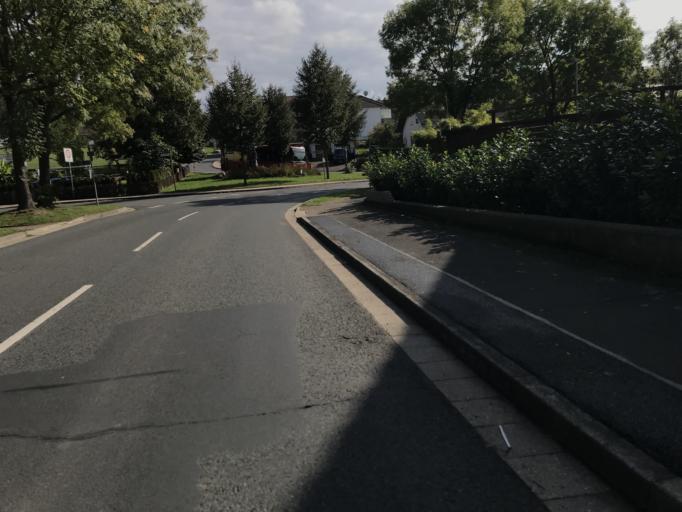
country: DE
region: Hesse
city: Gudensberg
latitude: 51.1660
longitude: 9.3759
